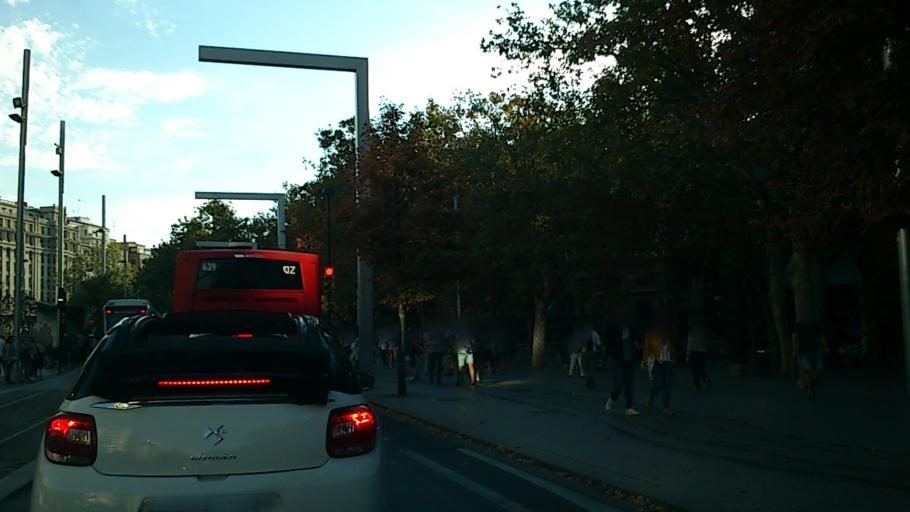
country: ES
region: Aragon
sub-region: Provincia de Zaragoza
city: Zaragoza
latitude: 41.6485
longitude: -0.8847
